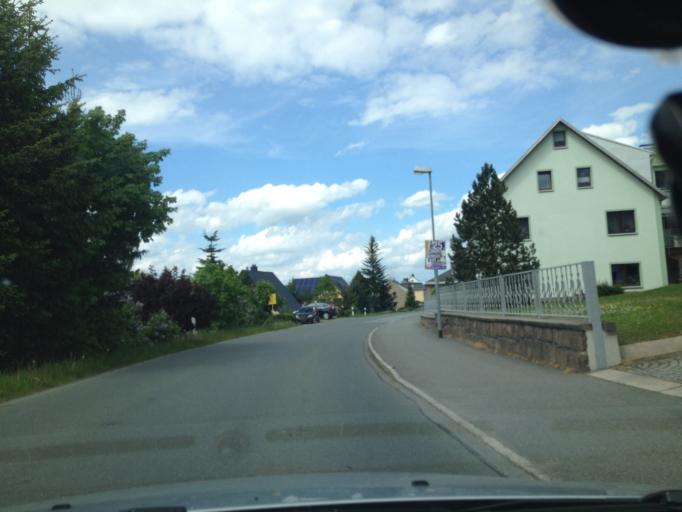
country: DE
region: Saxony
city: Barenstein
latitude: 50.5244
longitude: 12.9958
